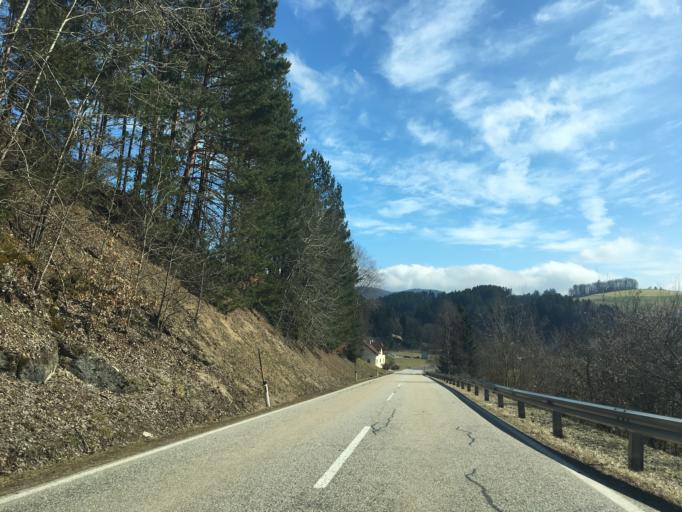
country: AT
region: Lower Austria
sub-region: Politischer Bezirk Melk
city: Dorfstetten
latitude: 48.2770
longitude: 14.9170
